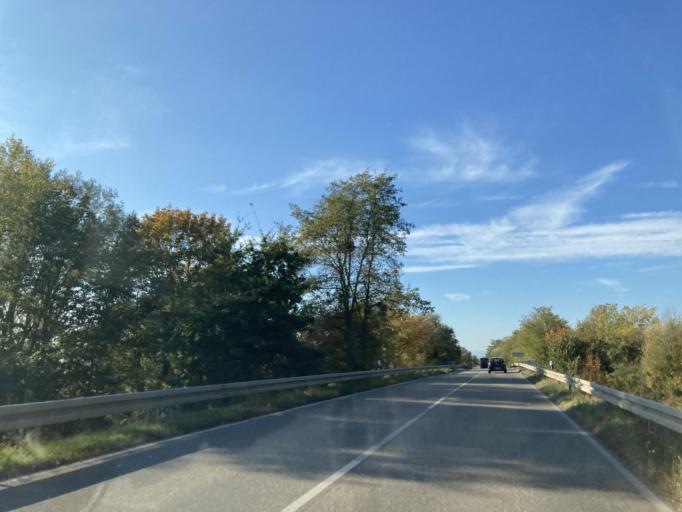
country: DE
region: Baden-Wuerttemberg
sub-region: Freiburg Region
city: Eschbach
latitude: 47.8867
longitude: 7.6221
